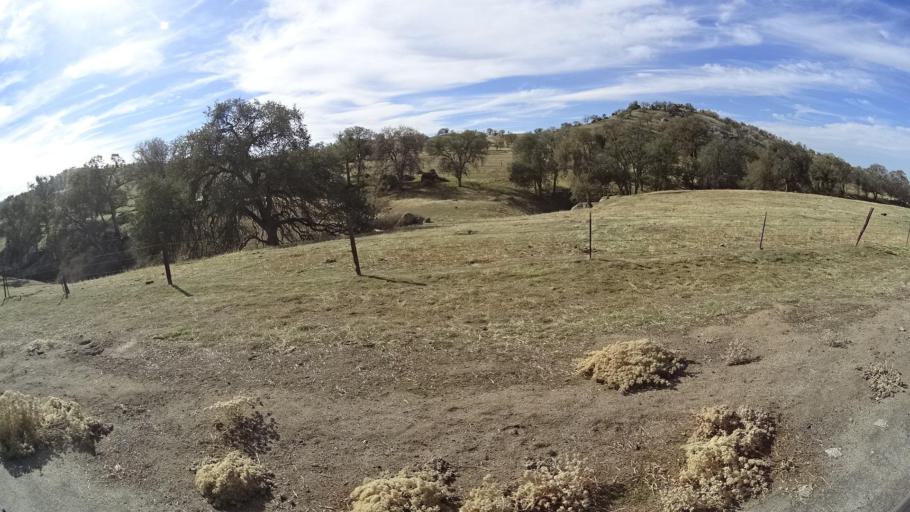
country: US
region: California
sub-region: Kern County
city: Oildale
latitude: 35.5815
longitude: -118.8152
